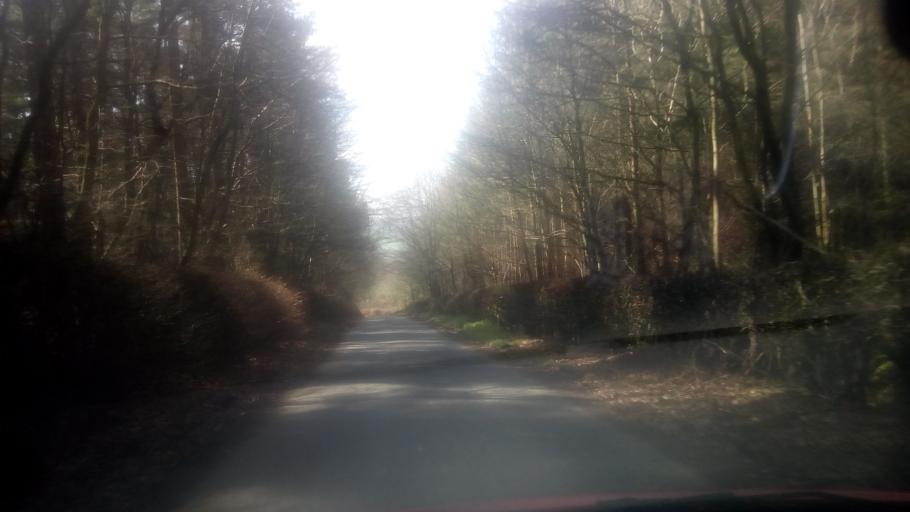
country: GB
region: Scotland
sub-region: The Scottish Borders
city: Jedburgh
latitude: 55.4820
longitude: -2.5224
